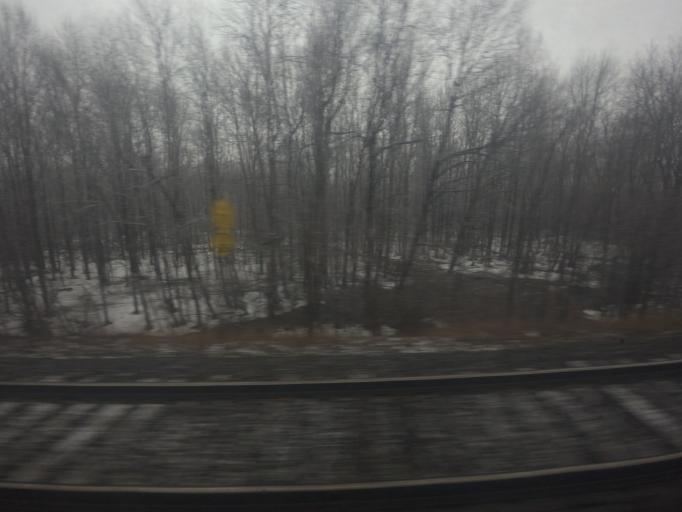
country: CA
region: Ontario
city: Brockville
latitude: 44.5698
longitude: -75.7615
